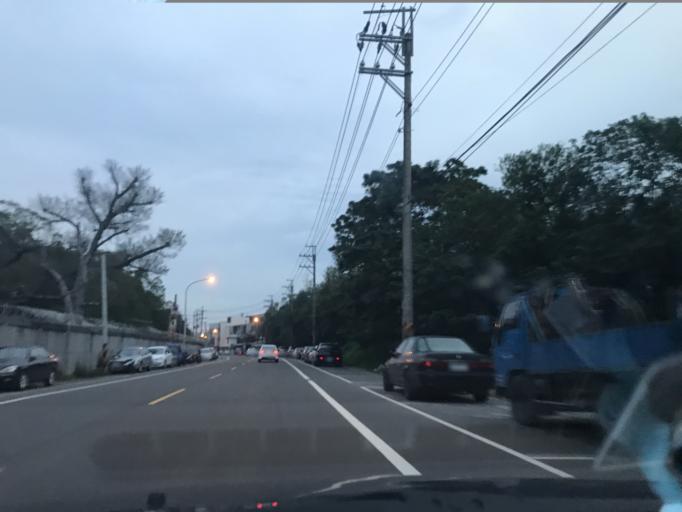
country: TW
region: Taiwan
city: Daxi
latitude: 24.9238
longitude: 121.2396
